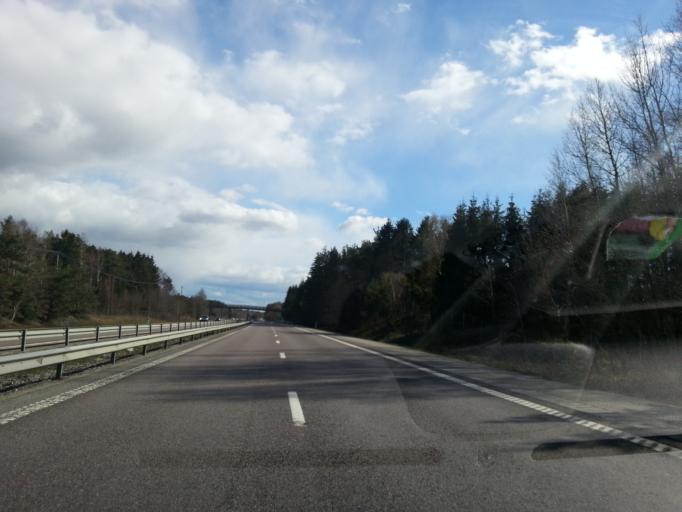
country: SE
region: Vaestra Goetaland
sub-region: Kungalvs Kommun
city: Kode
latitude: 57.9644
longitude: 11.8428
